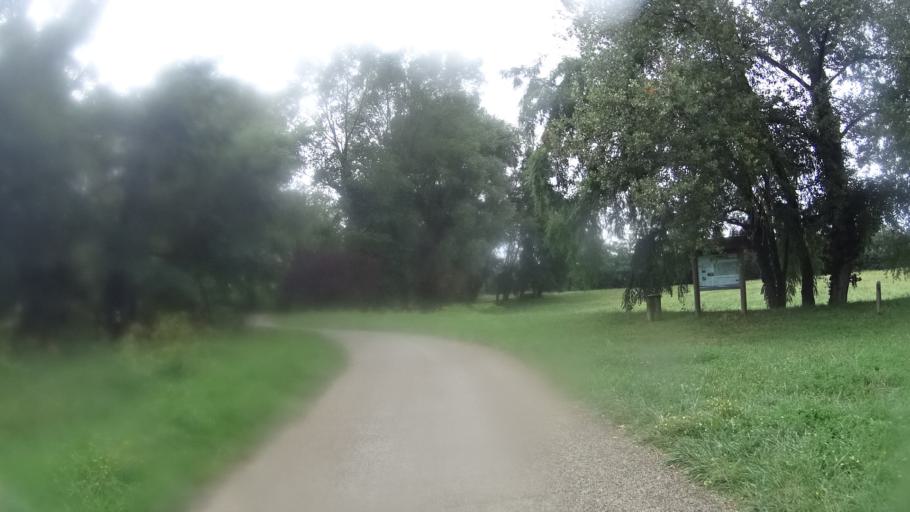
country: FR
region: Centre
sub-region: Departement du Loiret
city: Saint-Jean-le-Blanc
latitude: 47.8960
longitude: 1.9300
